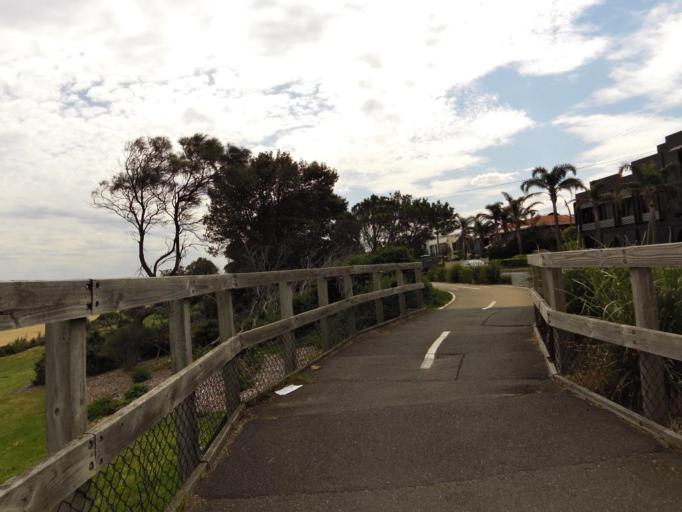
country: AU
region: Victoria
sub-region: Bayside
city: North Brighton
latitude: -37.9158
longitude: 144.9870
